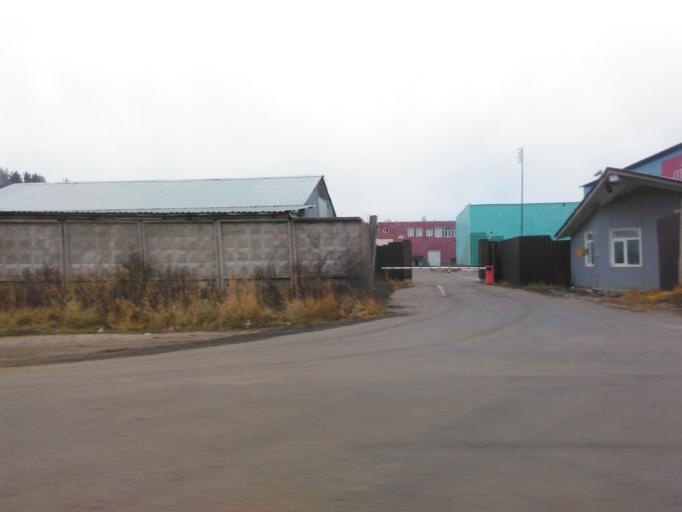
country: RU
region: Moskovskaya
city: Zelenogradskiy
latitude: 56.1128
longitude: 37.9562
